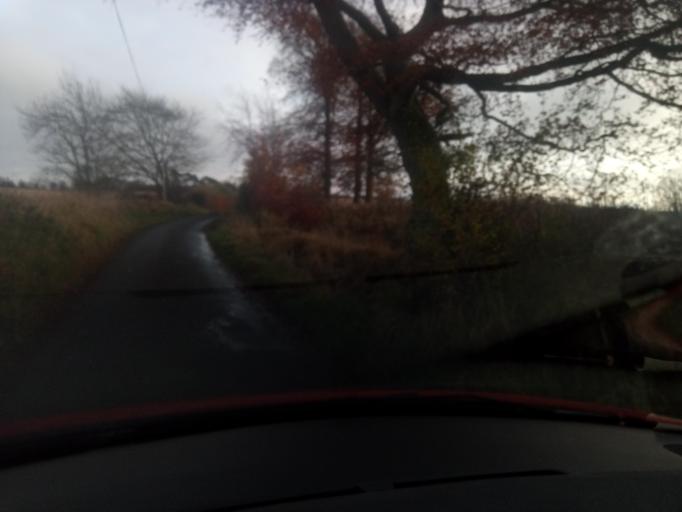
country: GB
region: Scotland
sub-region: The Scottish Borders
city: Jedburgh
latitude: 55.4871
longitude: -2.6131
